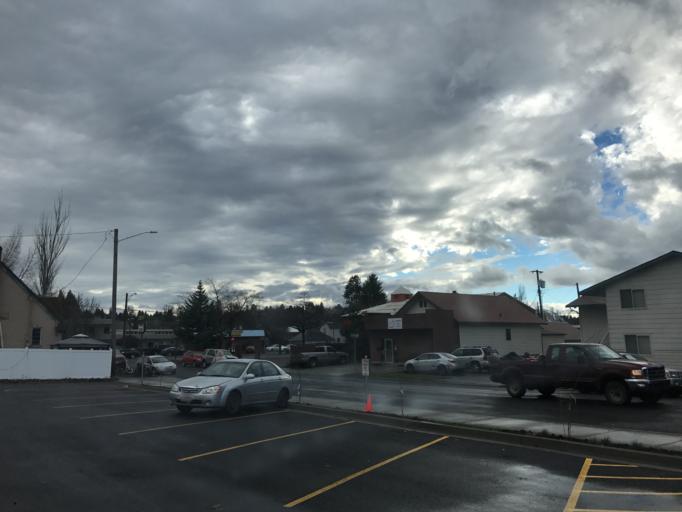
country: US
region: Idaho
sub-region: Latah County
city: Moscow
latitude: 46.7331
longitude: -117.0038
